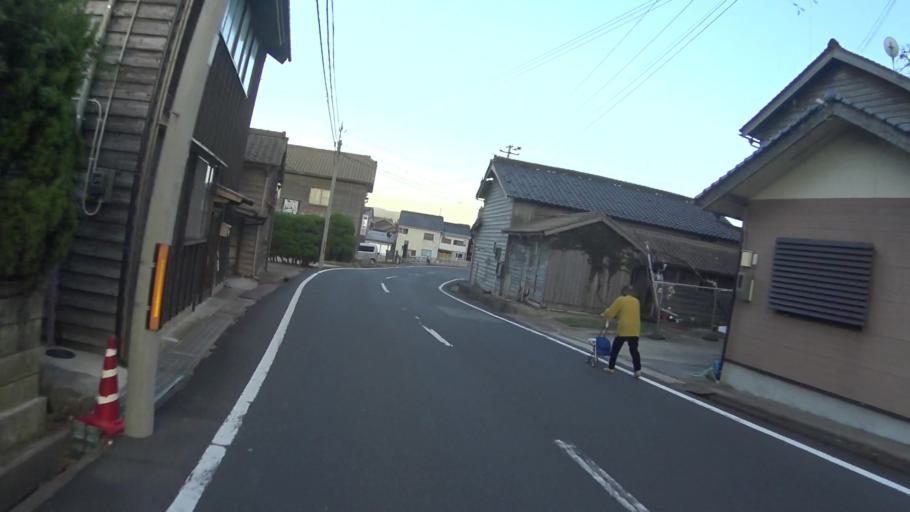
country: JP
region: Kyoto
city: Miyazu
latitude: 35.6900
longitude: 135.0162
